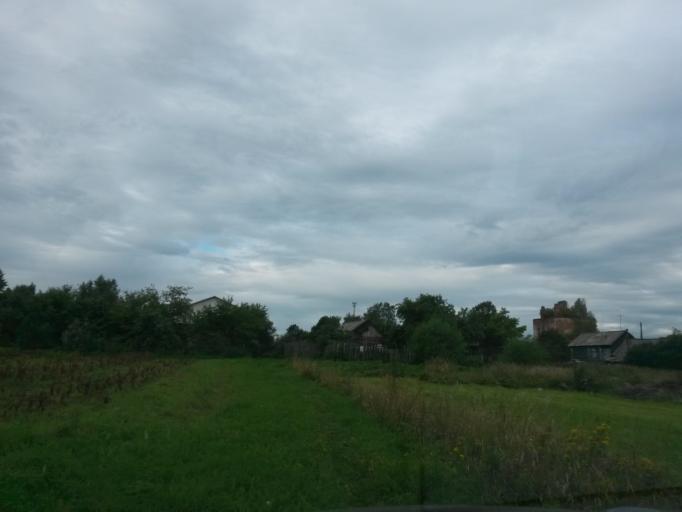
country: RU
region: Jaroslavl
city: Gavrilov-Yam
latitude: 57.3082
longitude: 39.9498
